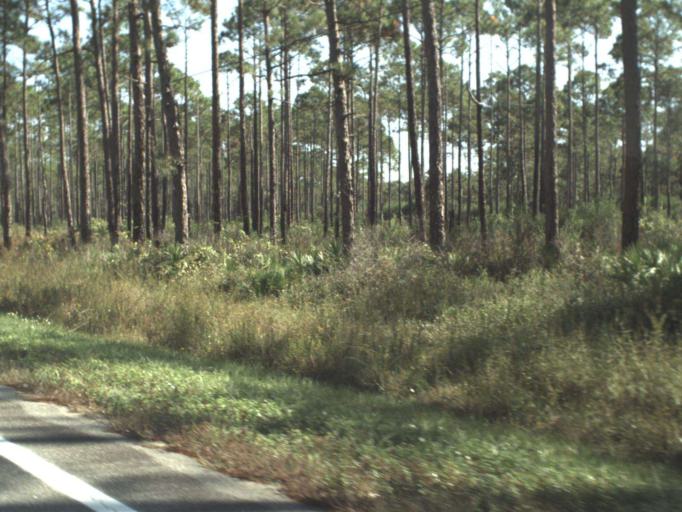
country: US
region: Florida
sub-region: Franklin County
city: Carrabelle
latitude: 29.9214
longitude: -84.4943
